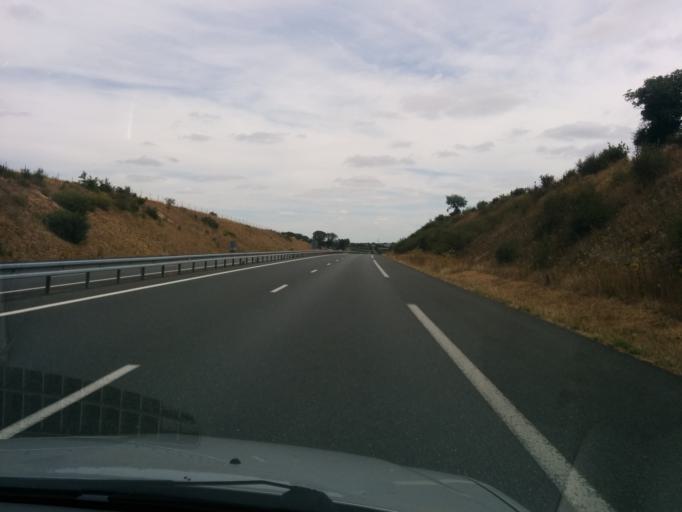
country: FR
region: Poitou-Charentes
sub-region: Departement des Deux-Sevres
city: Saint-Pierre-des-Echaubrognes
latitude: 46.9464
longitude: -0.7617
